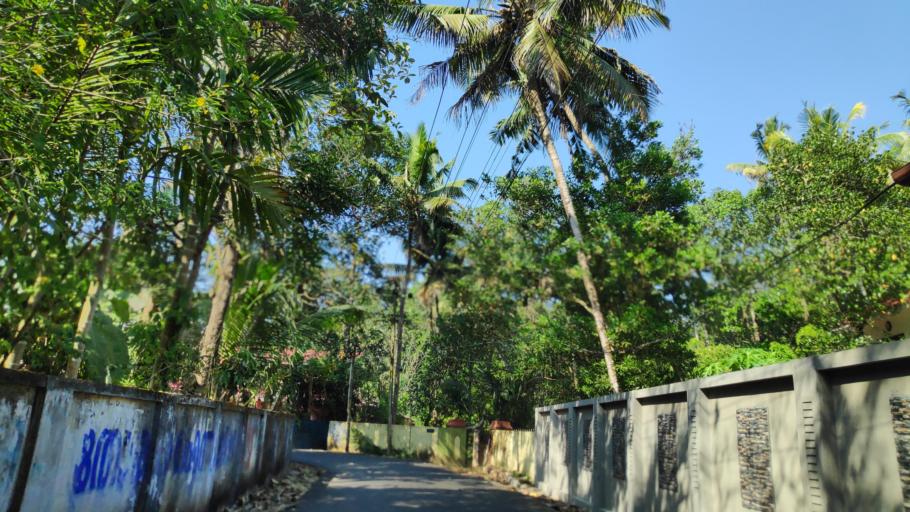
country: IN
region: Kerala
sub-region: Alappuzha
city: Alleppey
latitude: 9.5464
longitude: 76.3231
